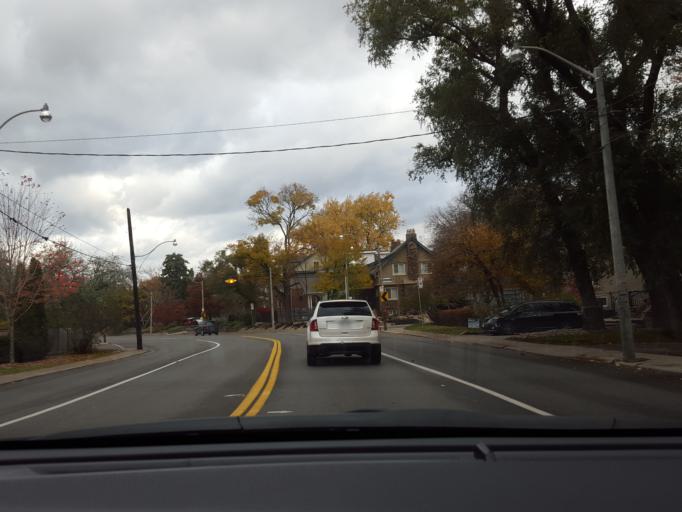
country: CA
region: Ontario
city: Toronto
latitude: 43.7154
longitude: -79.4120
